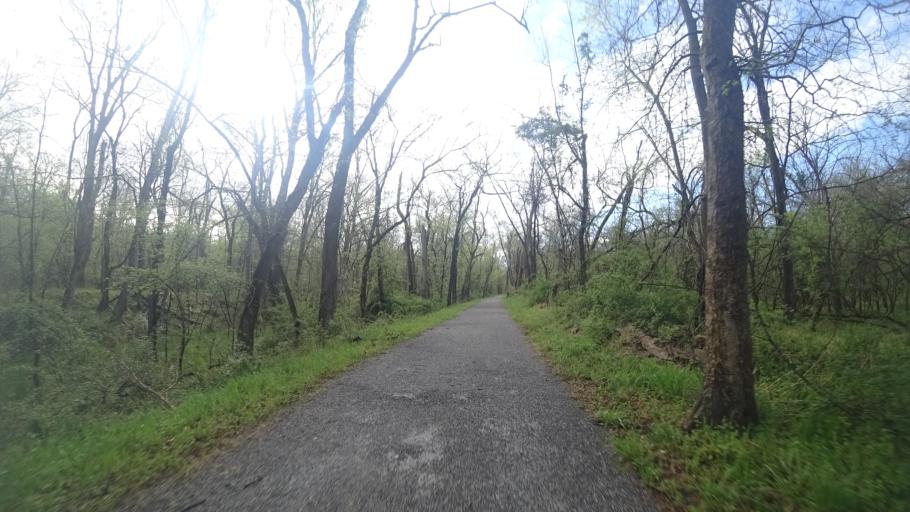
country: US
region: Virginia
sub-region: Loudoun County
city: Belmont
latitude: 39.1095
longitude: -77.4761
